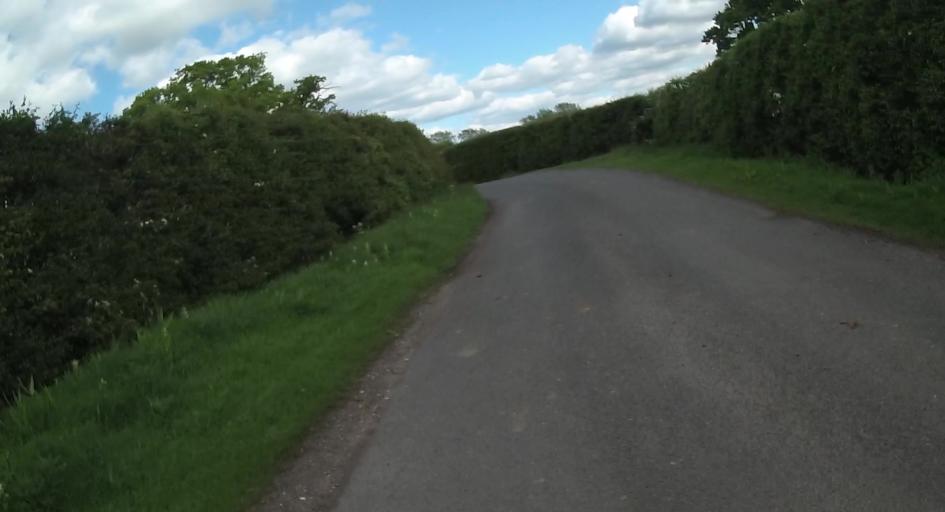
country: GB
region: England
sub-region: West Berkshire
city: Stratfield Mortimer
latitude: 51.3430
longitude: -1.0153
